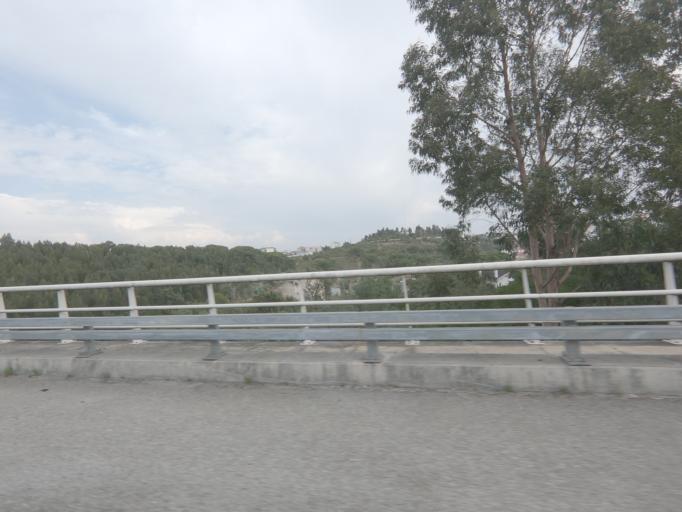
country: PT
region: Coimbra
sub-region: Coimbra
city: Coimbra
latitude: 40.2043
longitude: -8.4508
